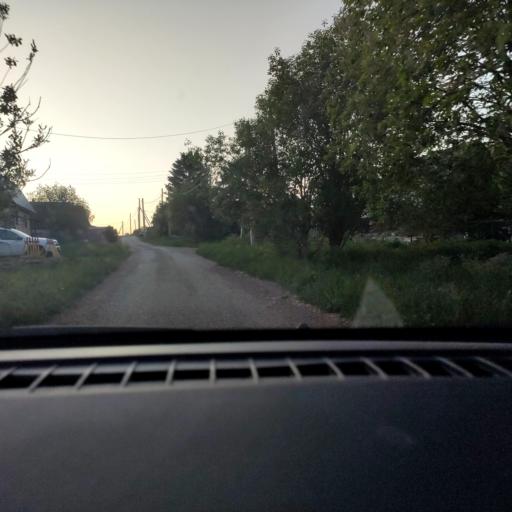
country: RU
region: Perm
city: Ferma
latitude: 57.9864
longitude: 56.3779
